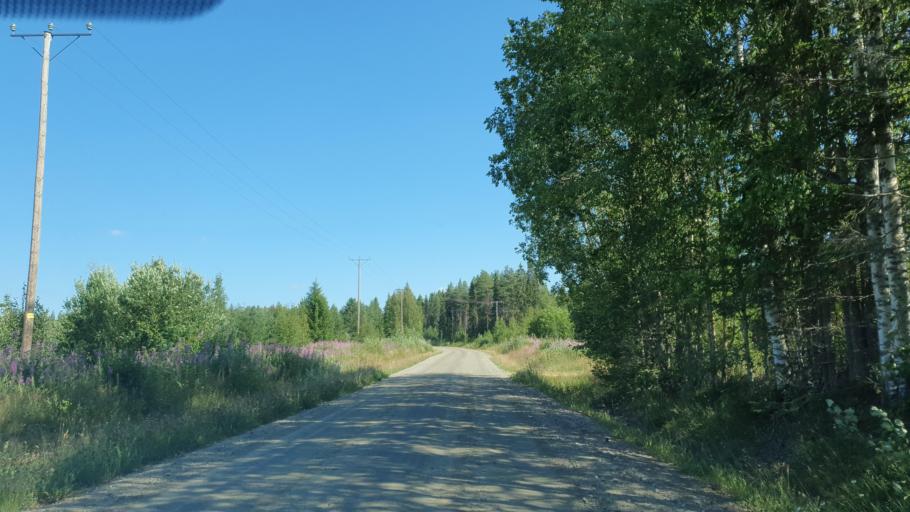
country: FI
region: Kainuu
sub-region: Kehys-Kainuu
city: Kuhmo
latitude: 64.0480
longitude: 29.6221
